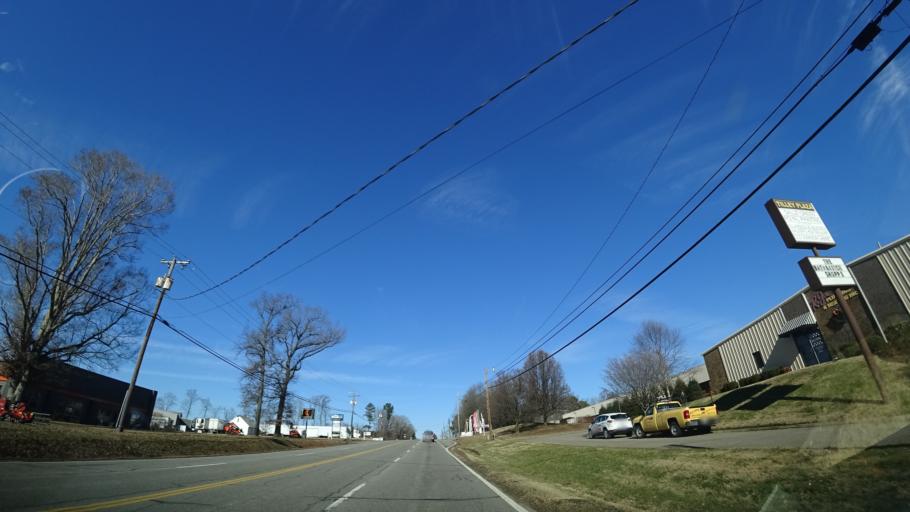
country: US
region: Virginia
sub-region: Henrico County
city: Glen Allen
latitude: 37.7022
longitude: -77.4646
